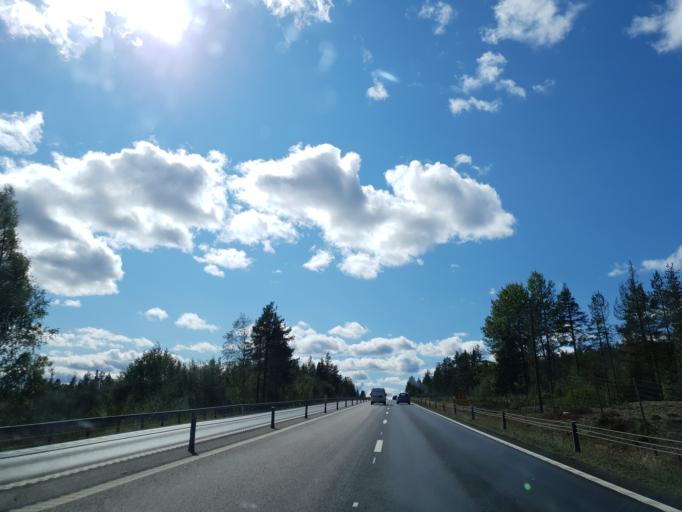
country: SE
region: Vaesterbotten
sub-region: Nordmalings Kommun
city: Nordmaling
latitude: 63.4936
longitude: 19.3185
